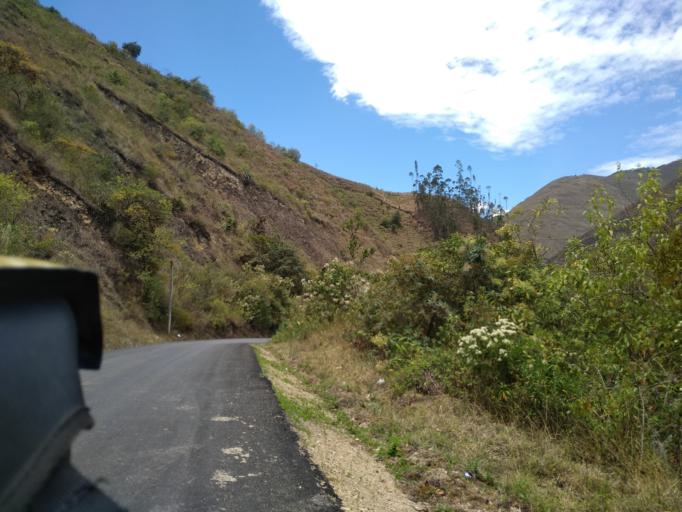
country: PE
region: Amazonas
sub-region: Provincia de Chachapoyas
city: Montevideo
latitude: -6.6485
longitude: -77.8024
